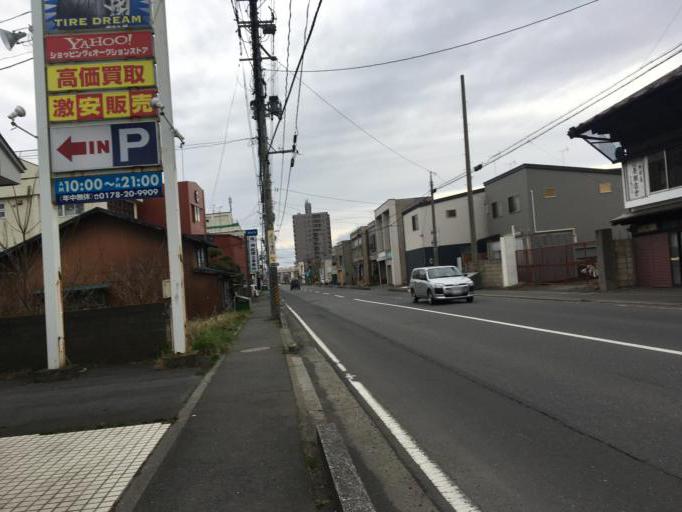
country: JP
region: Aomori
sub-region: Hachinohe Shi
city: Uchimaru
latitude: 40.5220
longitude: 141.5155
